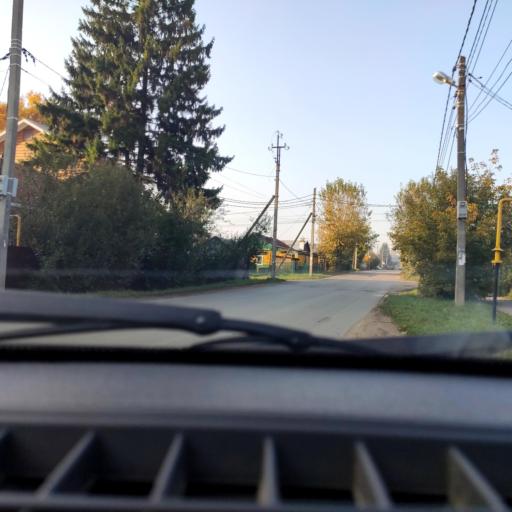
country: RU
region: Bashkortostan
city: Avdon
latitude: 54.6972
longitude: 55.8156
